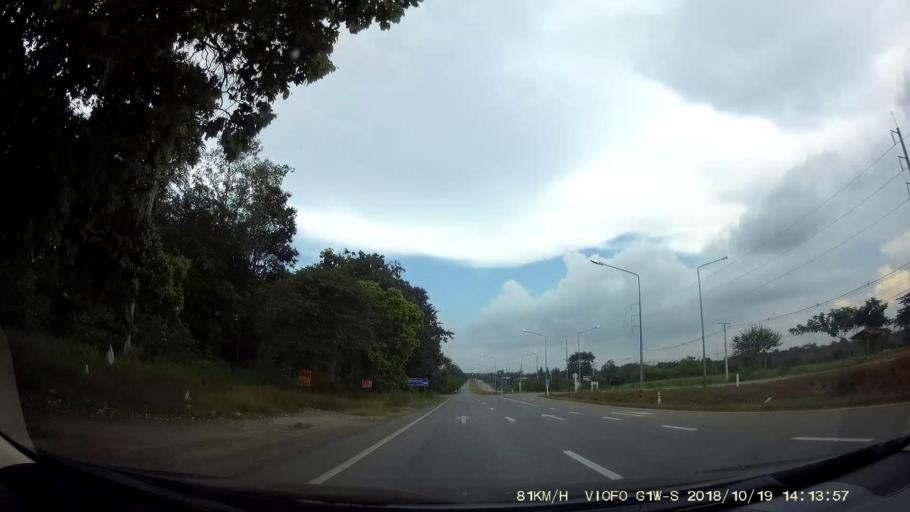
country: TH
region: Chaiyaphum
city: Khon Sawan
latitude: 15.9665
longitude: 102.1833
